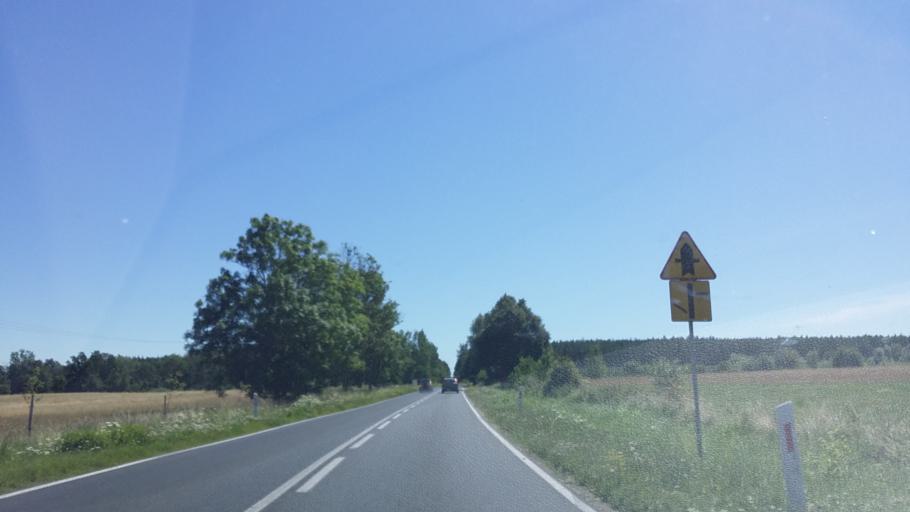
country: PL
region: West Pomeranian Voivodeship
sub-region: Powiat kolobrzeski
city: Kolobrzeg
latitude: 54.1269
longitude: 15.5748
